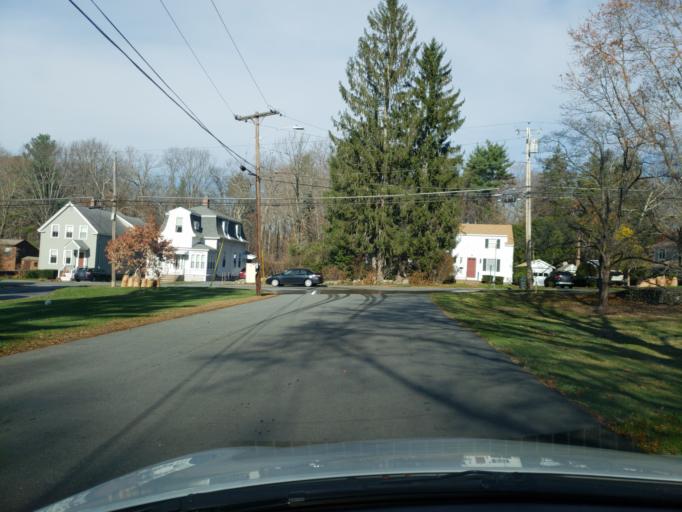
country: US
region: Massachusetts
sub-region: Essex County
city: Andover
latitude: 42.6594
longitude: -71.1265
